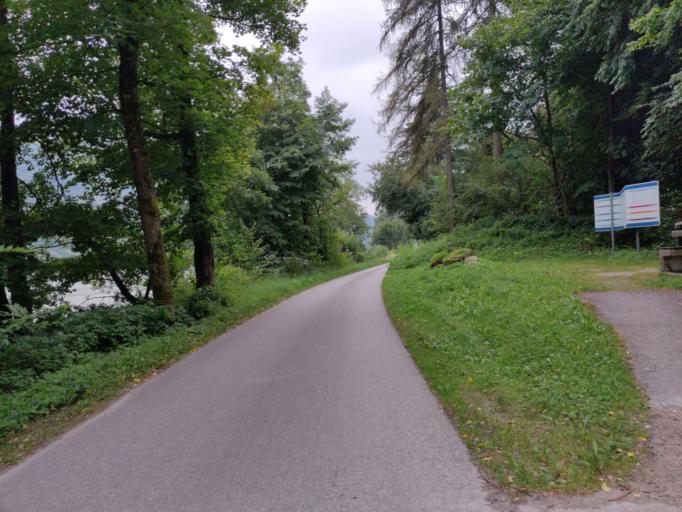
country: AT
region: Lower Austria
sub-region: Politischer Bezirk Melk
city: Nochling
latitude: 48.2286
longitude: 14.9397
